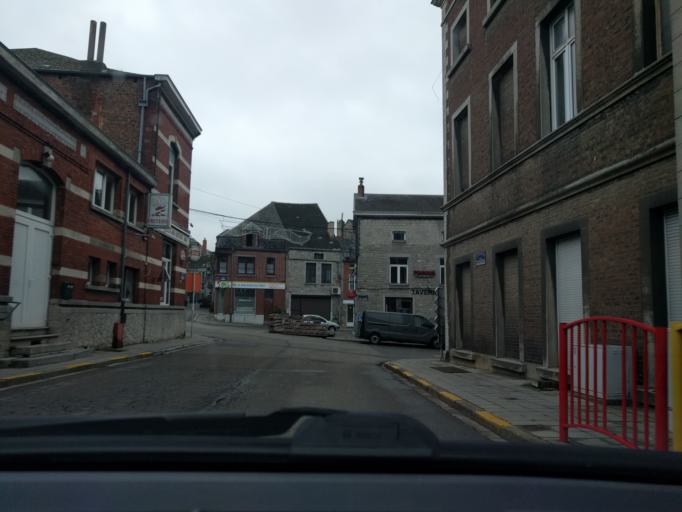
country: BE
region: Wallonia
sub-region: Province de Namur
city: Couvin
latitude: 50.0530
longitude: 4.4966
